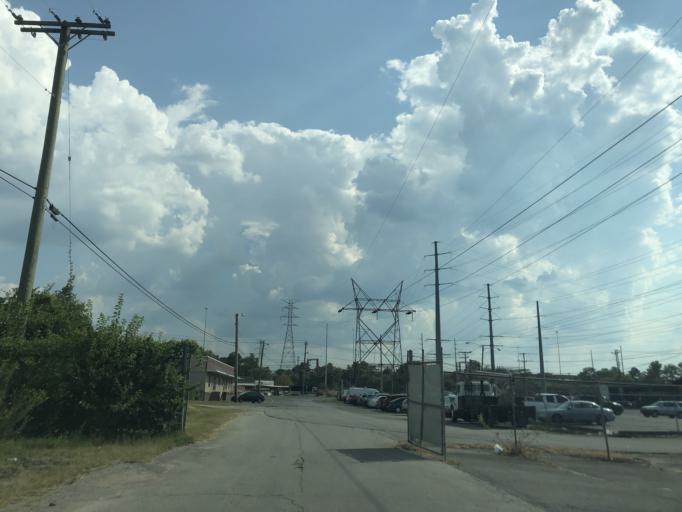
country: US
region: Tennessee
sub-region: Davidson County
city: Oak Hill
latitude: 36.1209
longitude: -86.7705
